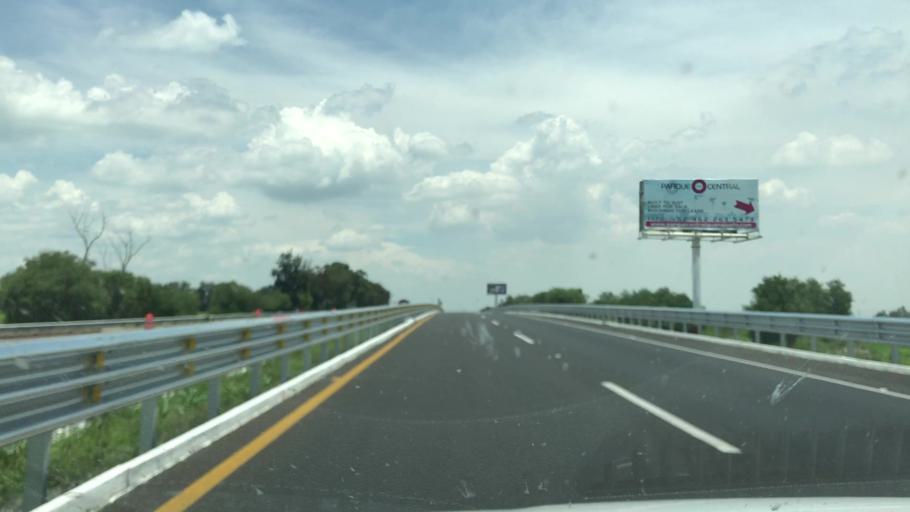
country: MX
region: Guanajuato
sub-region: Irapuato
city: Cuarta Brigada
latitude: 20.6506
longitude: -101.2829
